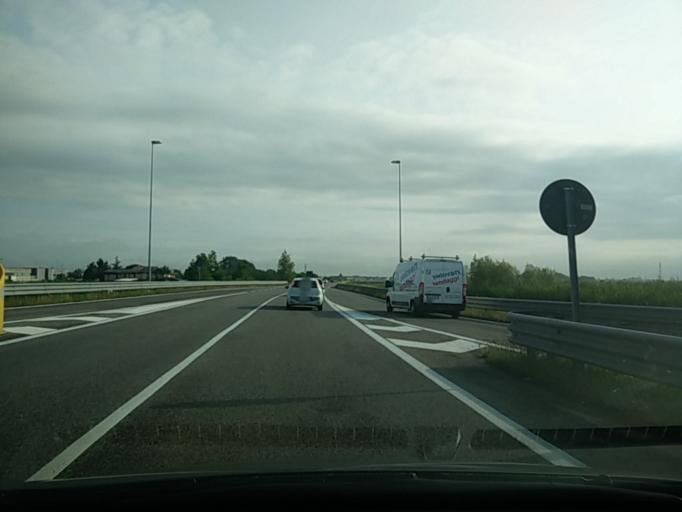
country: IT
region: Veneto
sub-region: Provincia di Venezia
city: Passarella
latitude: 45.6245
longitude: 12.6014
